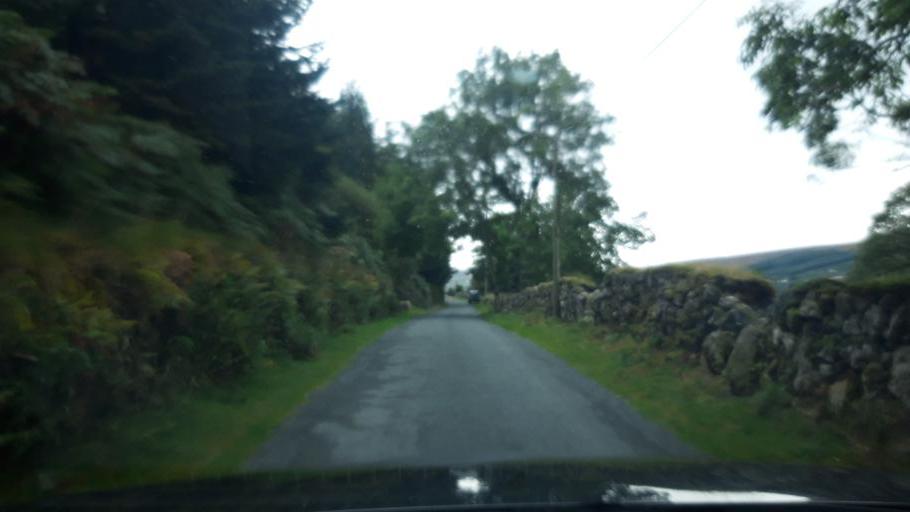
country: IE
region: Leinster
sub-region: Wicklow
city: Enniskerry
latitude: 53.1722
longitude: -6.2427
